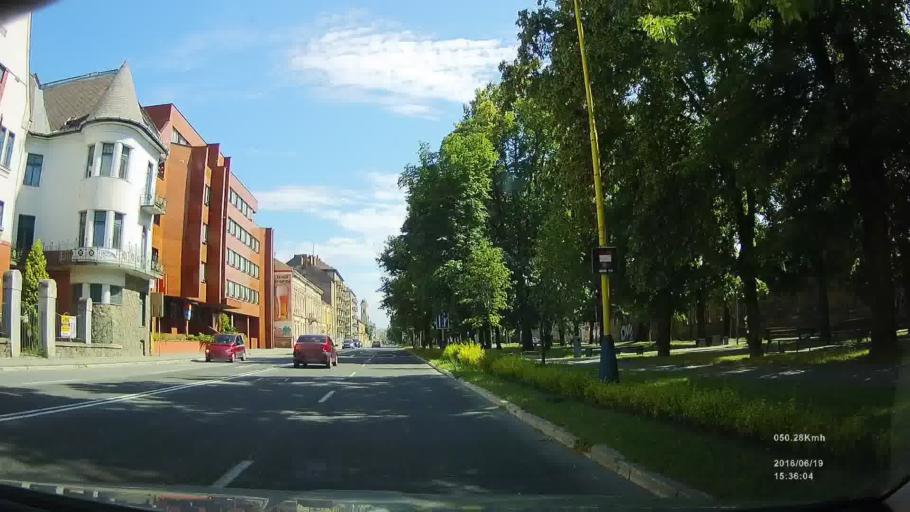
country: SK
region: Kosicky
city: Kosice
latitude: 48.7243
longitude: 21.2515
